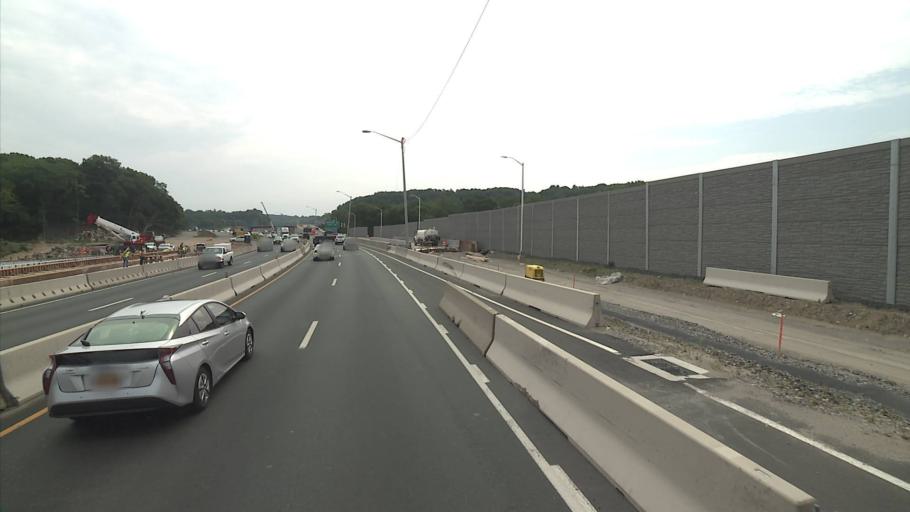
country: US
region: Connecticut
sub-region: New Haven County
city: Waterbury
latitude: 41.5399
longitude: -73.0182
